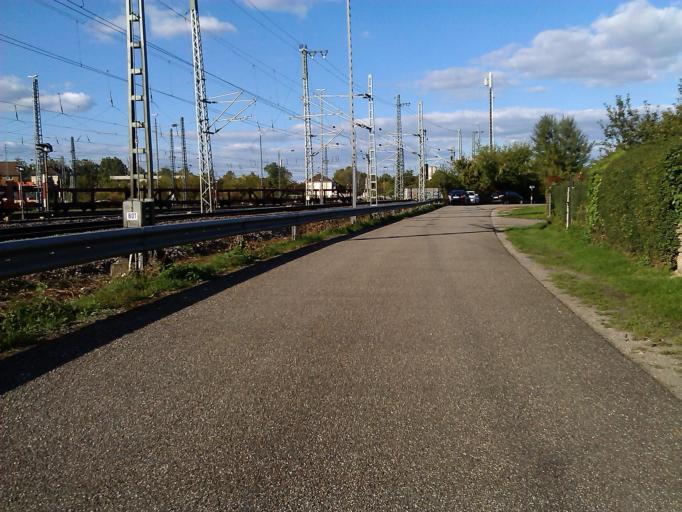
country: DE
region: Baden-Wuerttemberg
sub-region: Regierungsbezirk Stuttgart
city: Heilbronn
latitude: 49.1386
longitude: 9.1976
